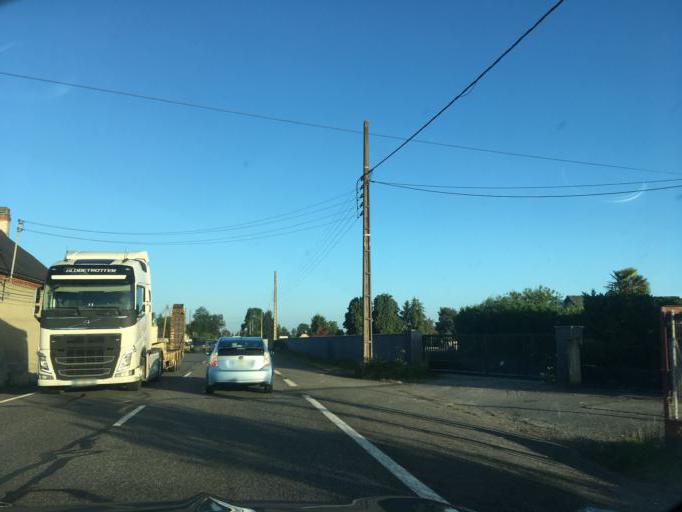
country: FR
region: Aquitaine
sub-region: Departement des Pyrenees-Atlantiques
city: Ger
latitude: 43.2468
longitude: -0.0438
